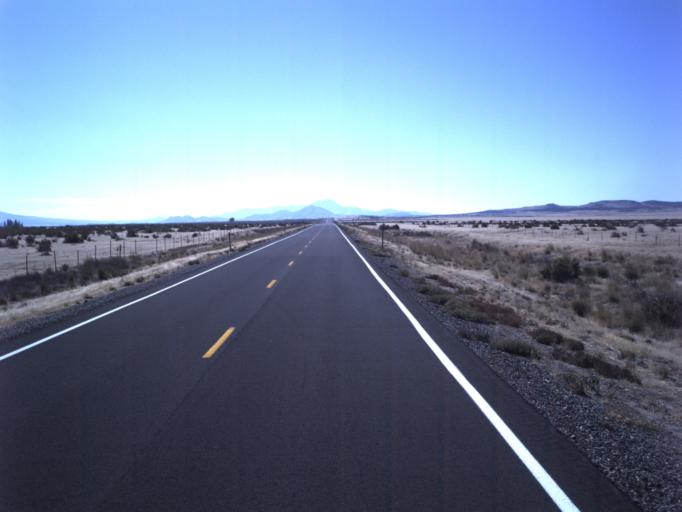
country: US
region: Utah
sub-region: Tooele County
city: Grantsville
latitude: 40.3237
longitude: -112.7440
